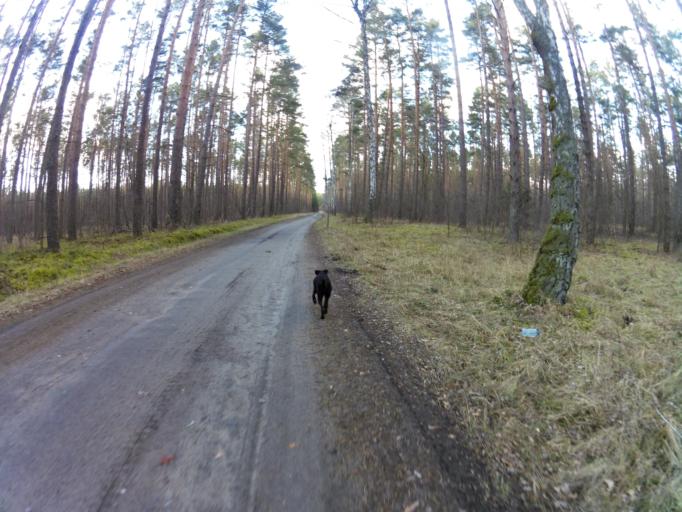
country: PL
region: West Pomeranian Voivodeship
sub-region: Powiat mysliborski
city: Debno
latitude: 52.7913
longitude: 14.7486
